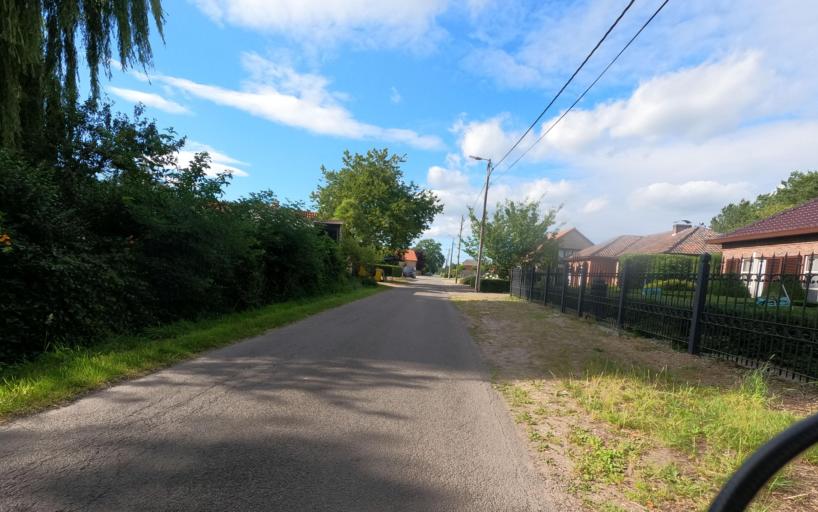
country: BE
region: Flanders
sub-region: Provincie Vlaams-Brabant
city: Tremelo
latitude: 51.0271
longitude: 4.7252
